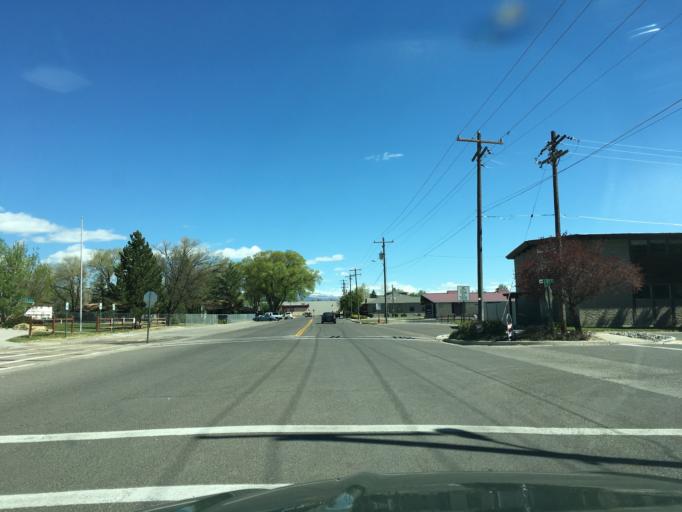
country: US
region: Colorado
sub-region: Montrose County
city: Montrose
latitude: 38.4719
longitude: -107.8683
